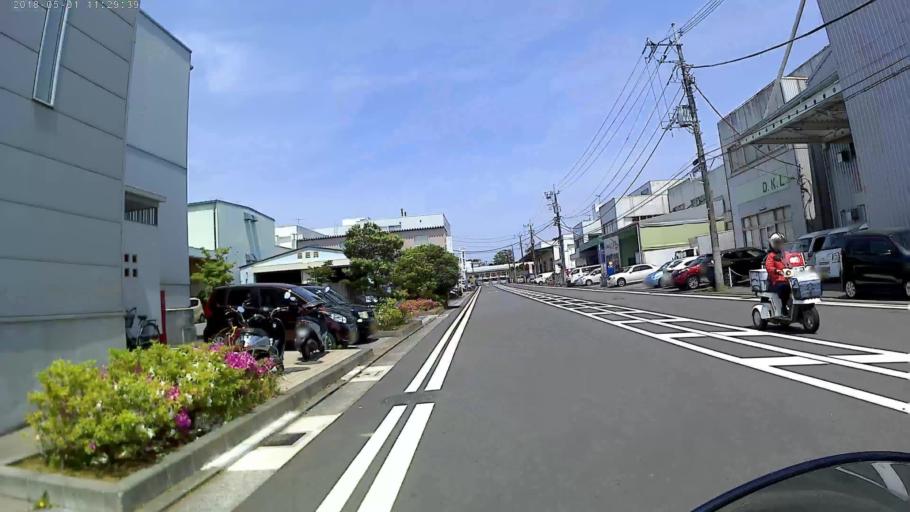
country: JP
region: Kanagawa
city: Minami-rinkan
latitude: 35.4988
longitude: 139.4872
